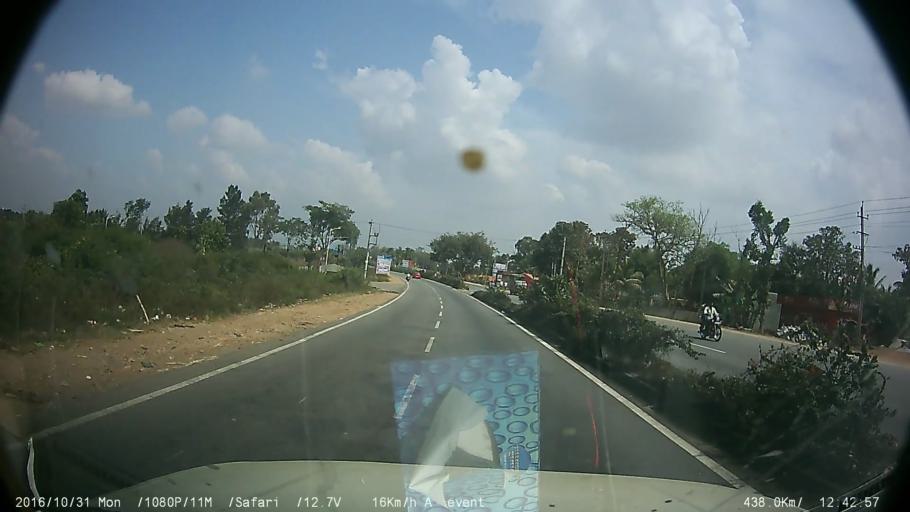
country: IN
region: Karnataka
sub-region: Mysore
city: Mysore
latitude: 12.3541
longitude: 76.5200
